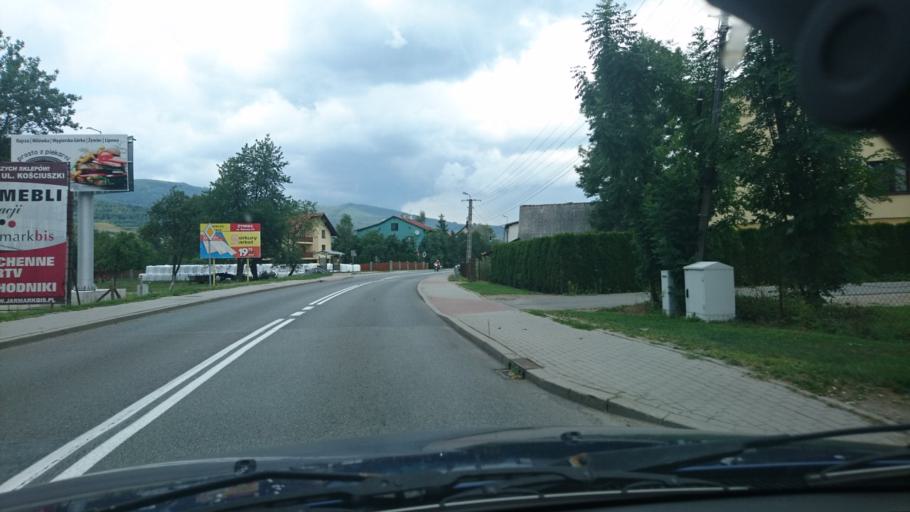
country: PL
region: Silesian Voivodeship
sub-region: Powiat zywiecki
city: Cisiec
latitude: 49.5808
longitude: 19.1009
